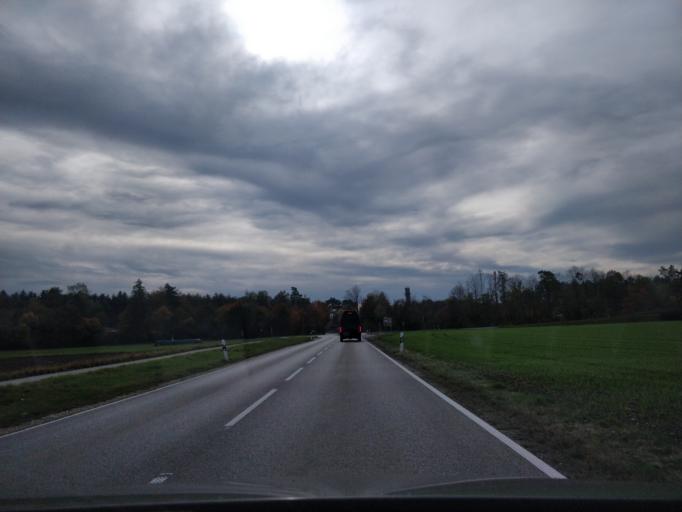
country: DE
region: Bavaria
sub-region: Swabia
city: Oberottmarshausen
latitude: 48.2231
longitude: 10.8681
